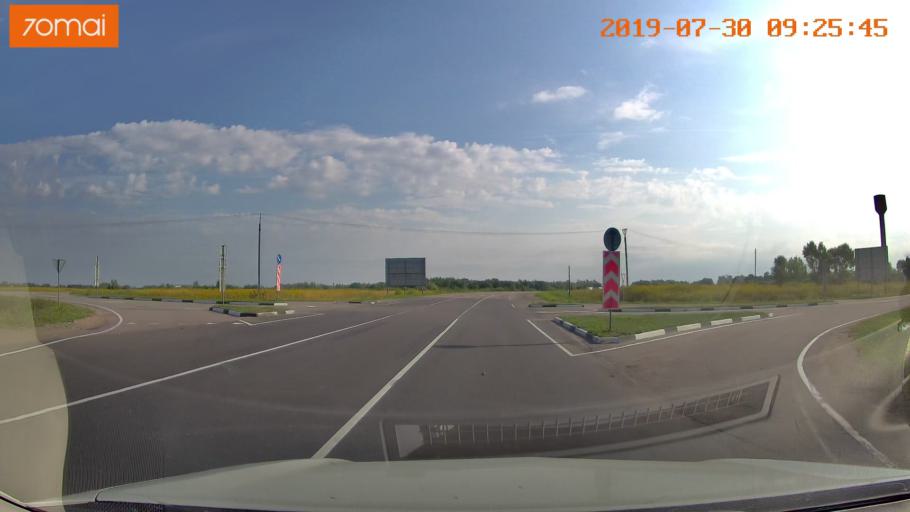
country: LT
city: Kybartai
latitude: 54.6429
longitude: 22.7214
